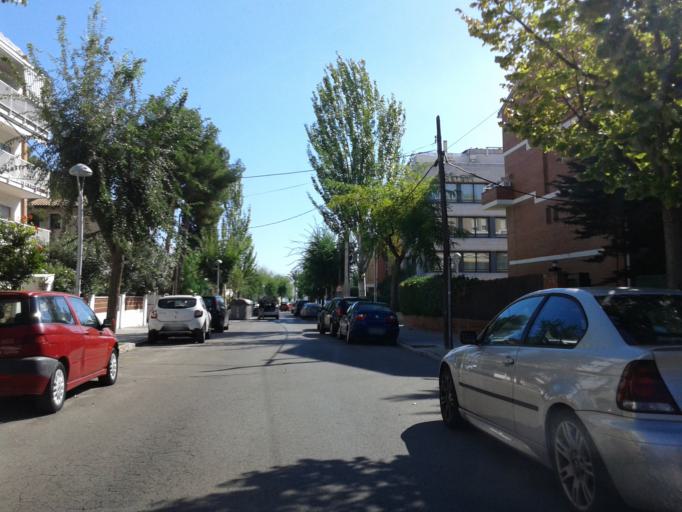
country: ES
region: Catalonia
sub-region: Provincia de Barcelona
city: Vilanova i la Geltru
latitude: 41.2150
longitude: 1.7212
